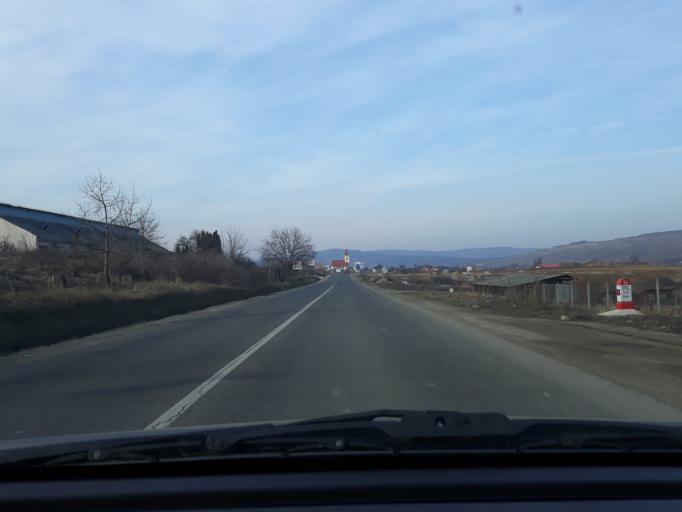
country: RO
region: Salaj
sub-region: Comuna Hereclean
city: Hereclean
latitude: 47.2329
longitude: 22.9965
